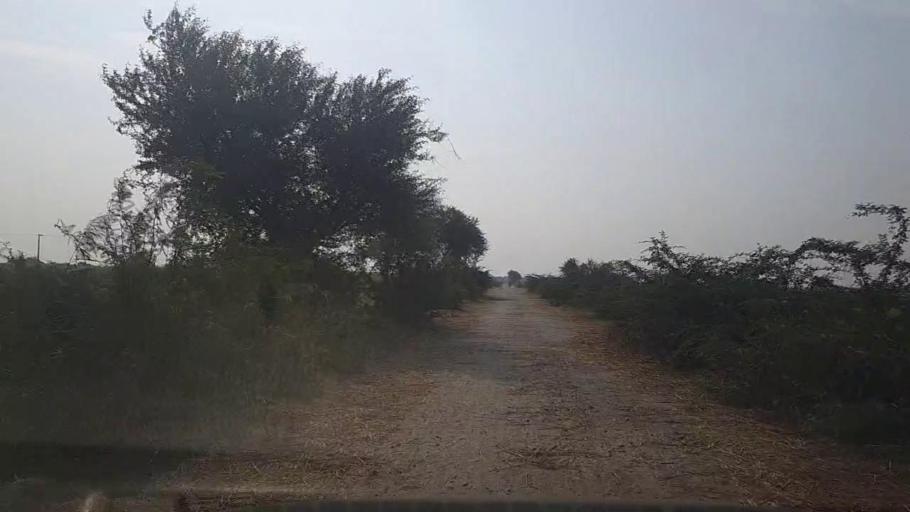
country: PK
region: Sindh
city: Bulri
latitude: 25.0149
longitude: 68.2997
